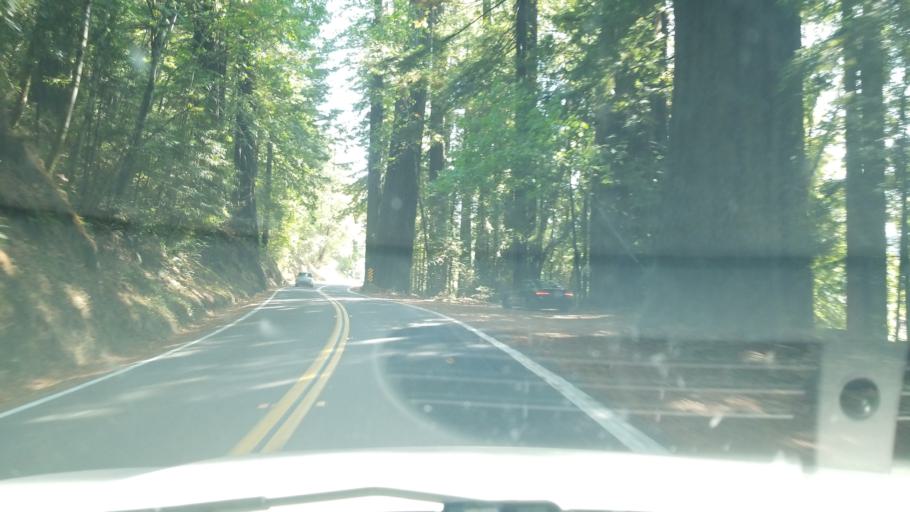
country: US
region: California
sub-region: Humboldt County
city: Redway
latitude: 40.2506
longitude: -123.8228
